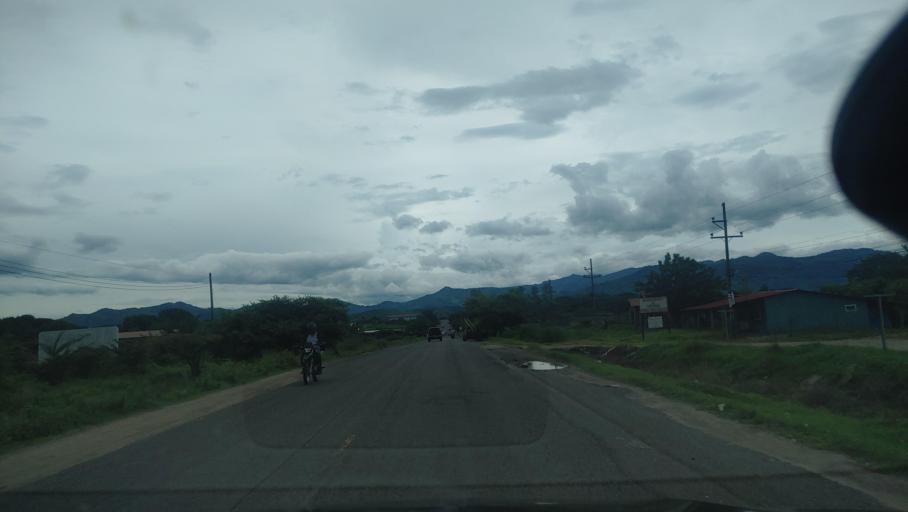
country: HN
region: Choluteca
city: Santa Ana de Yusguare
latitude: 13.3351
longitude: -87.1334
